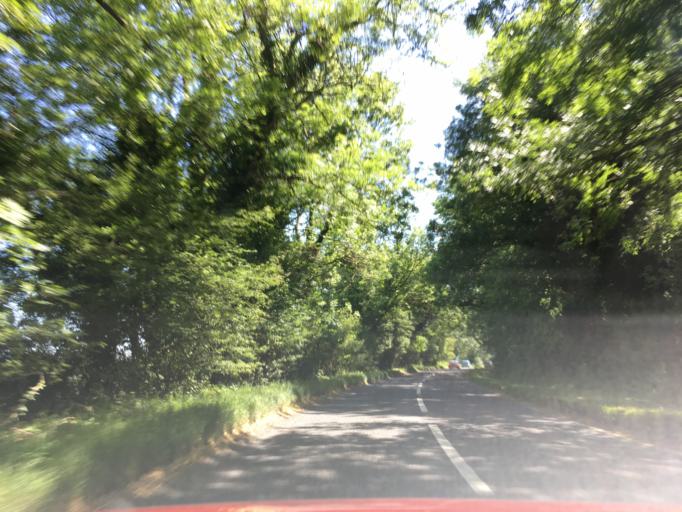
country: GB
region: England
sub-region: Gloucestershire
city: Stow on the Wold
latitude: 51.9292
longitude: -1.6920
